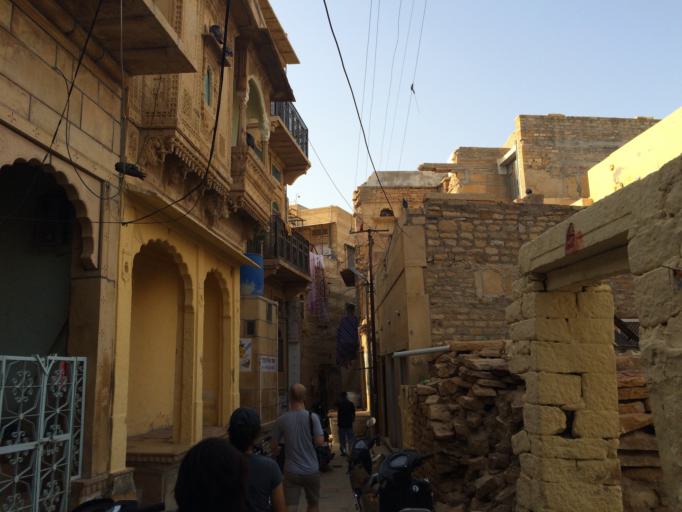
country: IN
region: Rajasthan
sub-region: Jaisalmer
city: Jaisalmer
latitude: 26.9138
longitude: 70.9128
